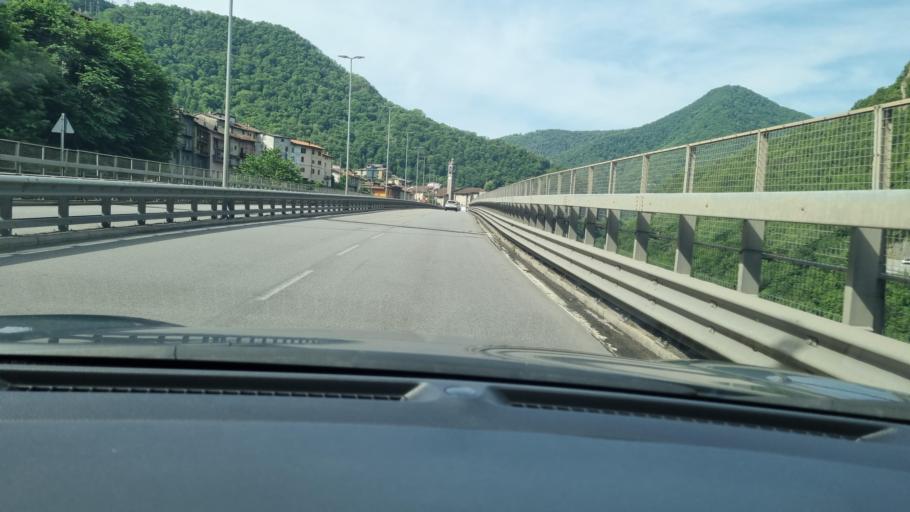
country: IT
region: Lombardy
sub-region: Provincia di Bergamo
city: Sedrina
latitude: 45.7849
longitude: 9.6283
